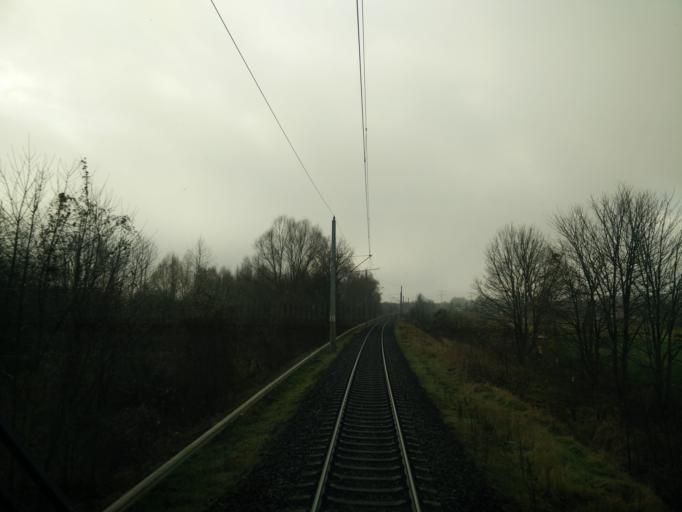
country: DE
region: Mecklenburg-Vorpommern
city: Wismar
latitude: 53.8858
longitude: 11.4759
